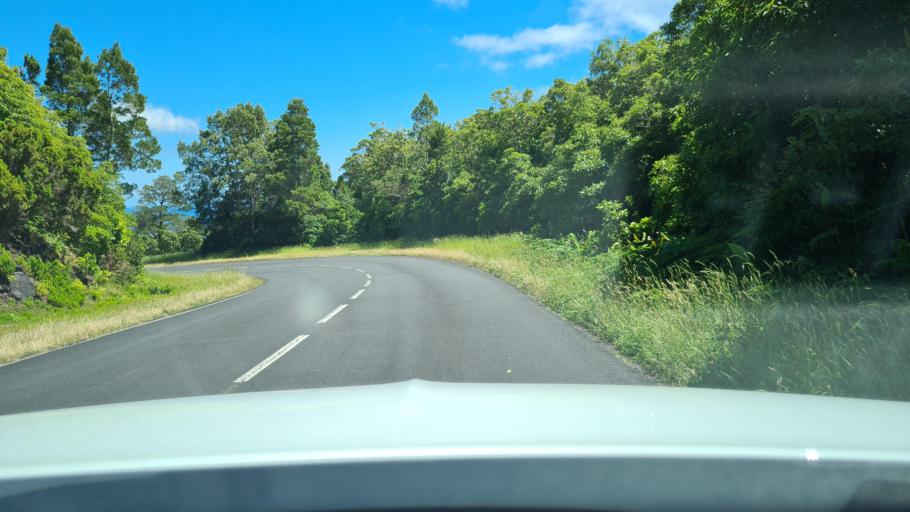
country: PT
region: Azores
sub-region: Sao Roque do Pico
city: Sao Roque do Pico
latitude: 38.4269
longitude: -28.2909
